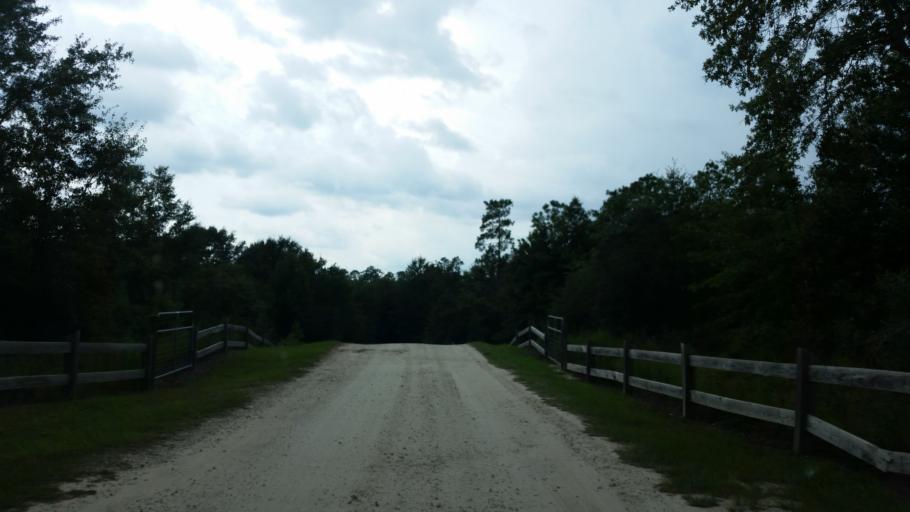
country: US
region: Florida
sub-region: Escambia County
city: Cantonment
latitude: 30.6767
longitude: -87.4042
